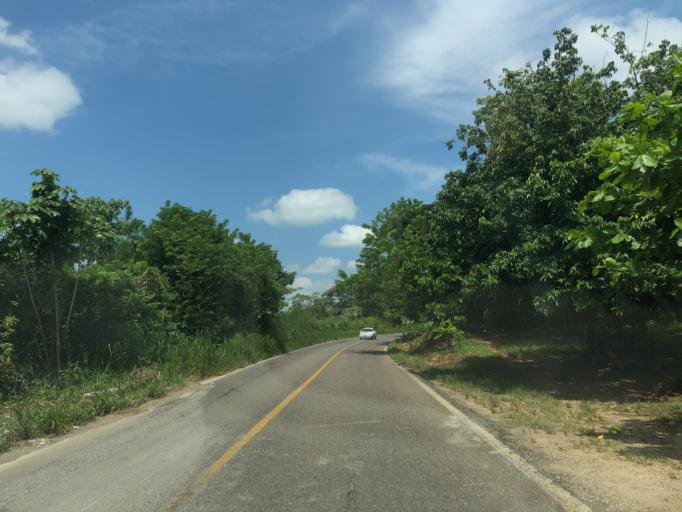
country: MX
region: Tabasco
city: Chontalpa
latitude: 17.5748
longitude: -93.5281
